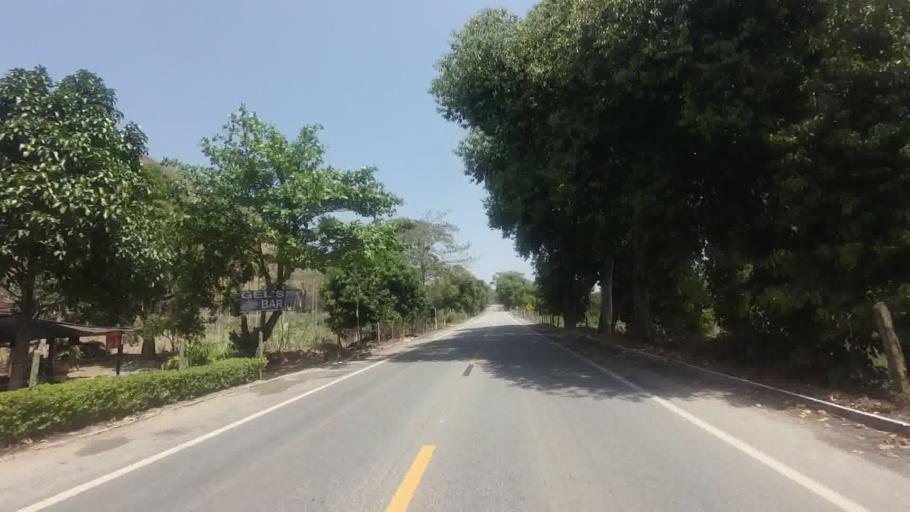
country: BR
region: Espirito Santo
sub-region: Cachoeiro De Itapemirim
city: Cachoeiro de Itapemirim
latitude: -20.8578
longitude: -41.2503
